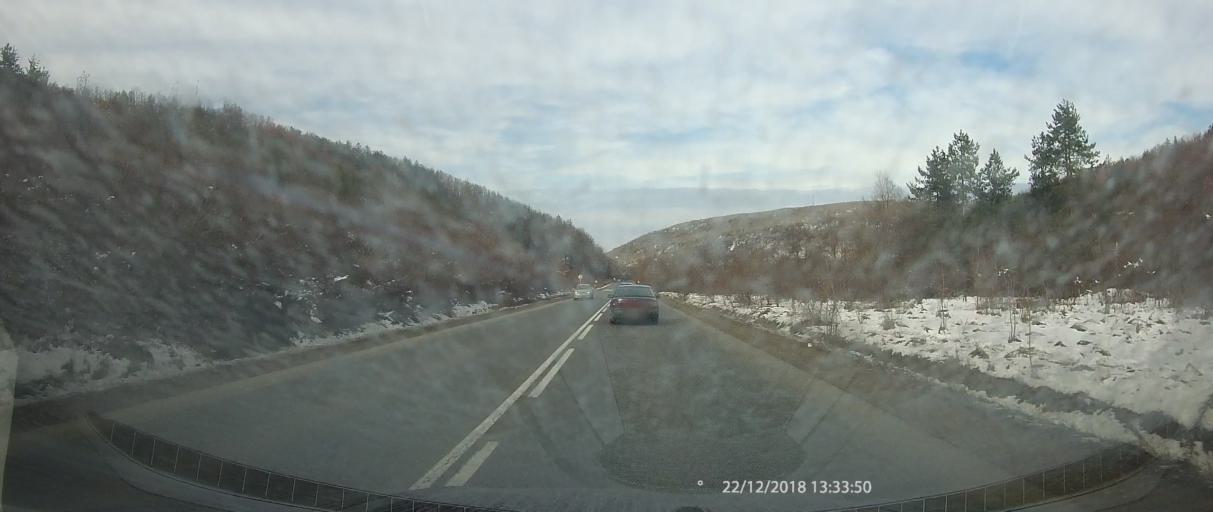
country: BG
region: Lovech
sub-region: Obshtina Lukovit
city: Lukovit
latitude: 43.1136
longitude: 24.1490
